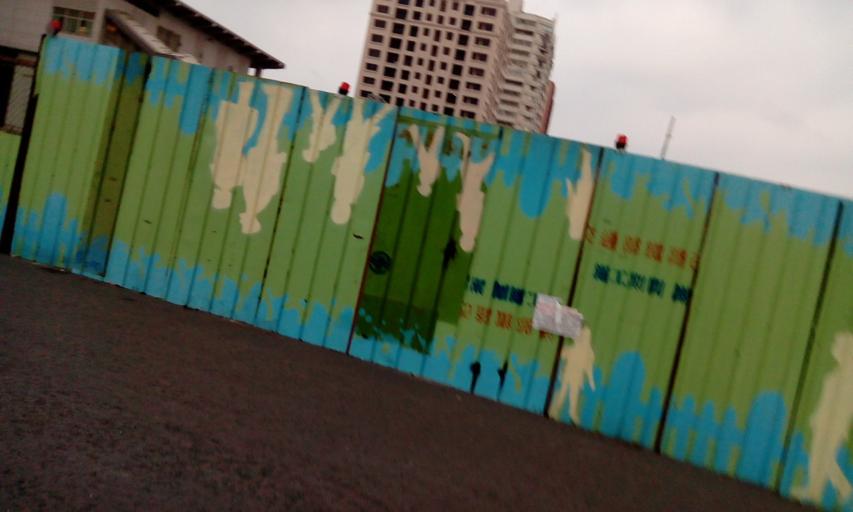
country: TW
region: Kaohsiung
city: Kaohsiung
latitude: 22.6753
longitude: 120.2945
